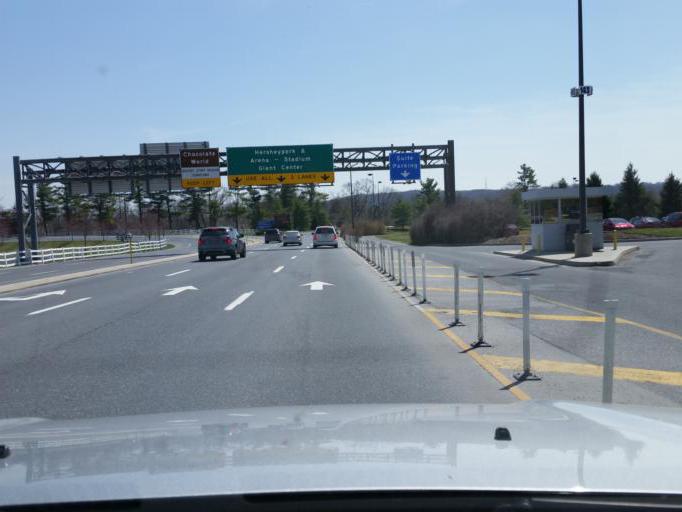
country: US
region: Pennsylvania
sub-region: Dauphin County
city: Hershey
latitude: 40.2873
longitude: -76.6678
